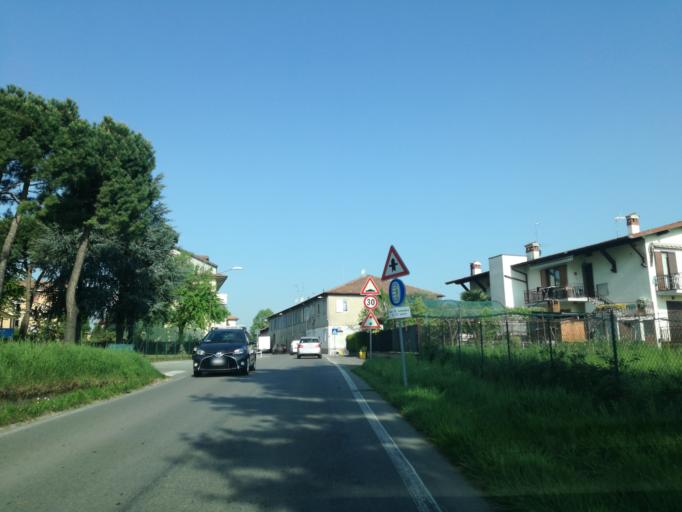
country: IT
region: Lombardy
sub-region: Provincia di Monza e Brianza
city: Ronco Briantino
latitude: 45.6765
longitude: 9.4121
